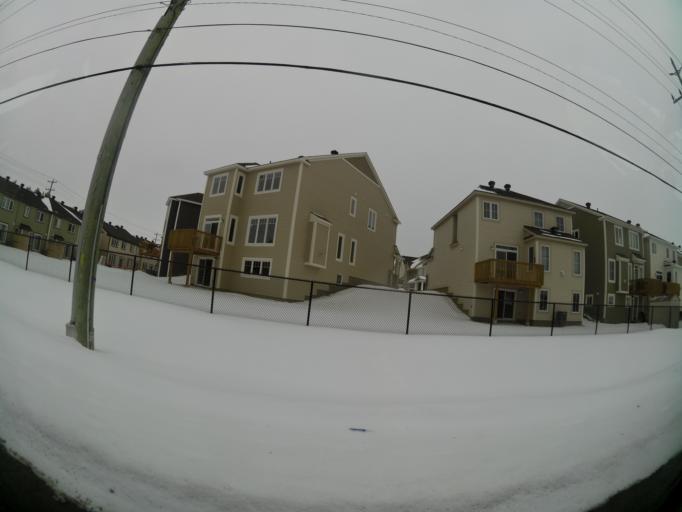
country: CA
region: Ontario
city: Bells Corners
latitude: 45.2828
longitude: -75.9286
